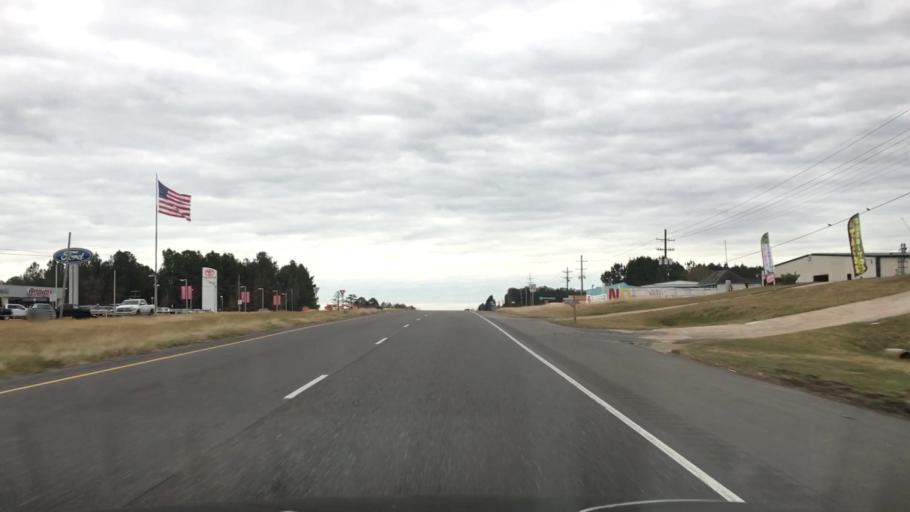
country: US
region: Louisiana
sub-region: Vernon Parish
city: New Llano
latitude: 31.0892
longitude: -93.2710
